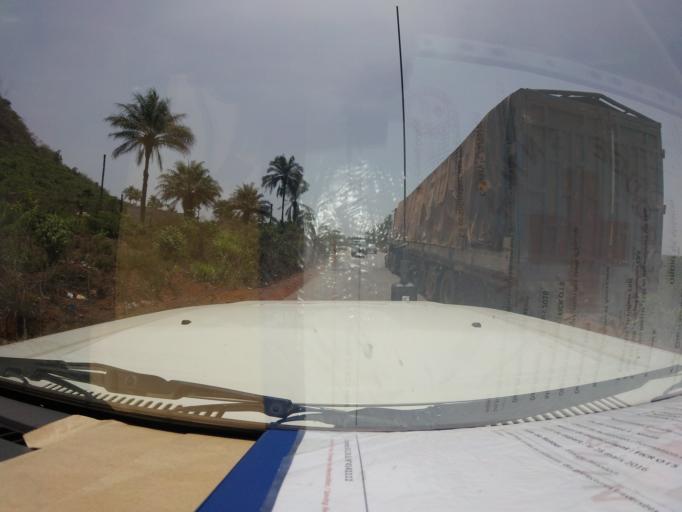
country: GN
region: Kindia
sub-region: Coyah
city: Coyah
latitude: 9.7839
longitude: -13.3328
